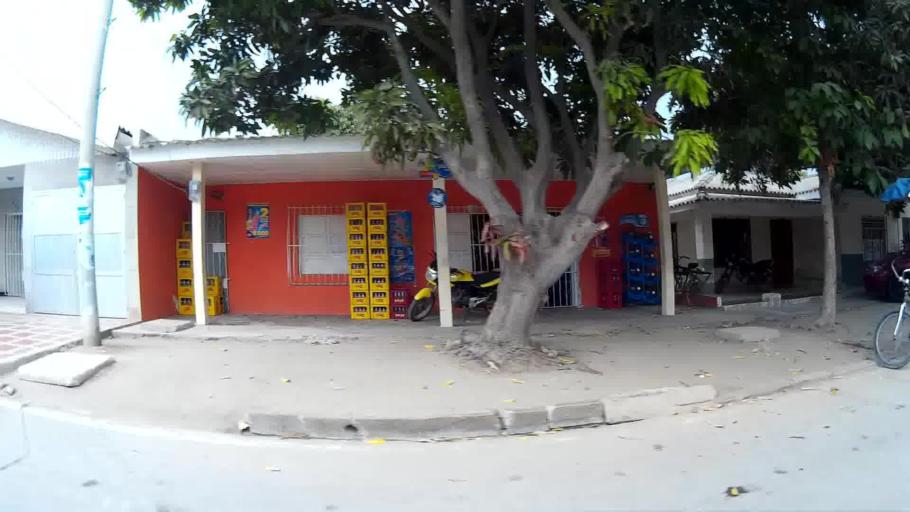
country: CO
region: Magdalena
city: Cienaga
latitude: 11.0134
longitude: -74.2454
